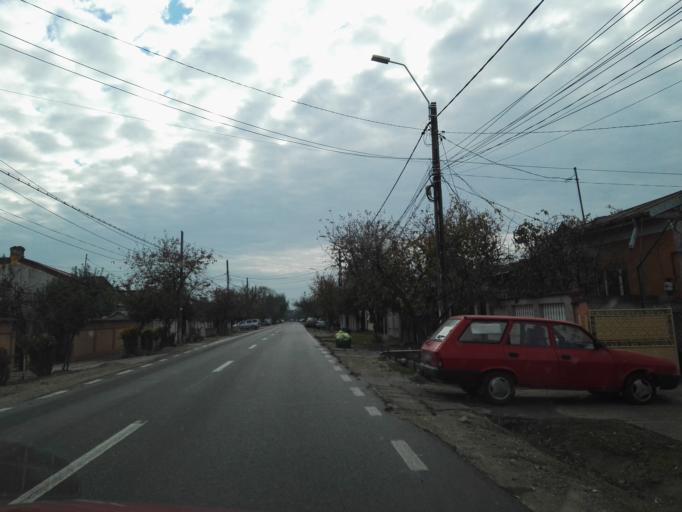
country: RO
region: Ilfov
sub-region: Comuna Magurele
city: Alunisu
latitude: 44.3403
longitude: 26.0527
